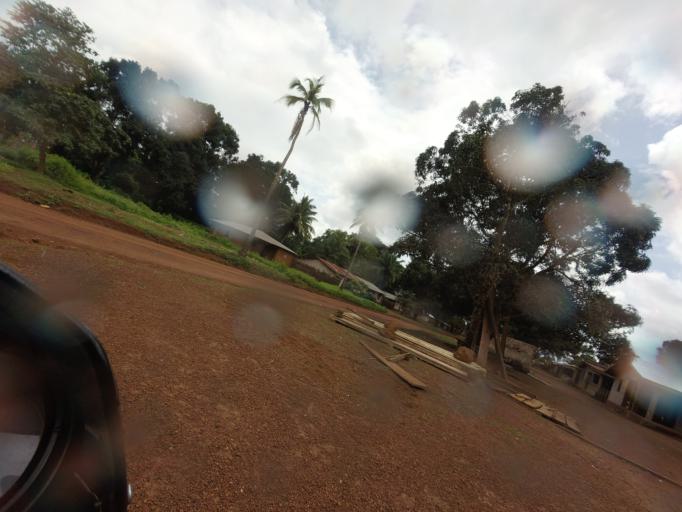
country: SL
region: Northern Province
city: Kukuna
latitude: 9.2717
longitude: -12.7059
